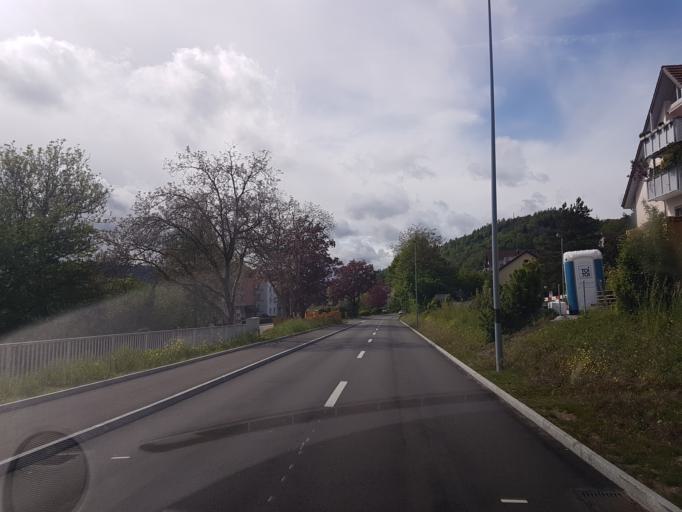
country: CH
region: Zurich
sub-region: Bezirk Dietikon
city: Geroldswil
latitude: 47.4278
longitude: 8.3947
